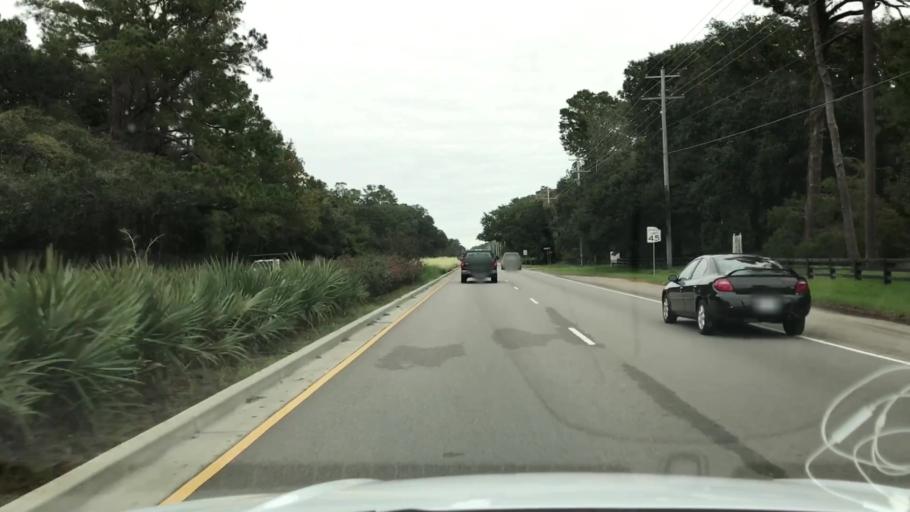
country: US
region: South Carolina
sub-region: Georgetown County
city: Murrells Inlet
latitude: 33.4518
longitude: -79.1180
